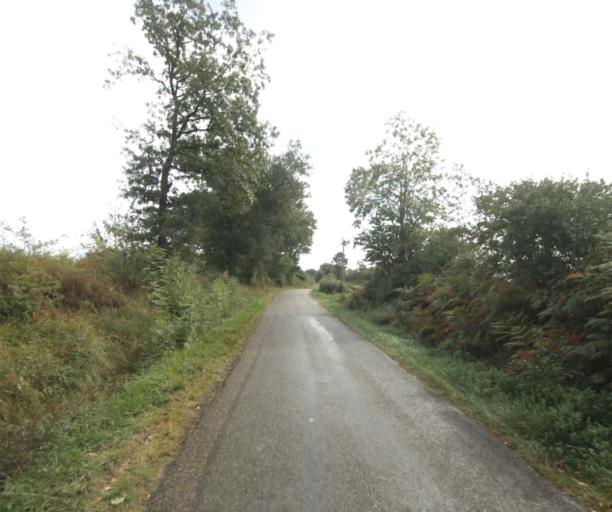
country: FR
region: Midi-Pyrenees
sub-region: Departement du Gers
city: Cazaubon
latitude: 43.8962
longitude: -0.1234
